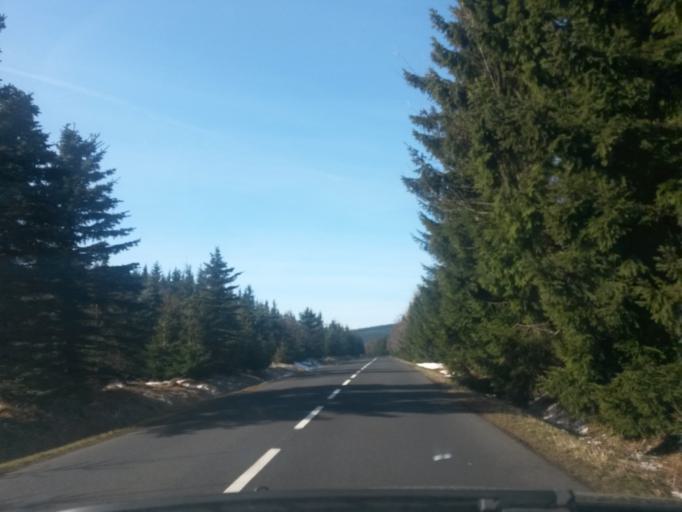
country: CZ
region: Ustecky
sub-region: Okres Chomutov
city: Kovarska
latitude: 50.4089
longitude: 13.0174
